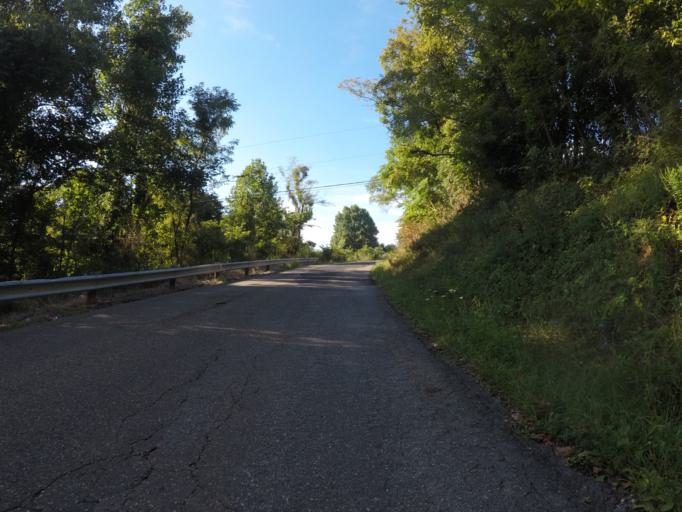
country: US
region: West Virginia
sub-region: Cabell County
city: Huntington
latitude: 38.4569
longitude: -82.4605
